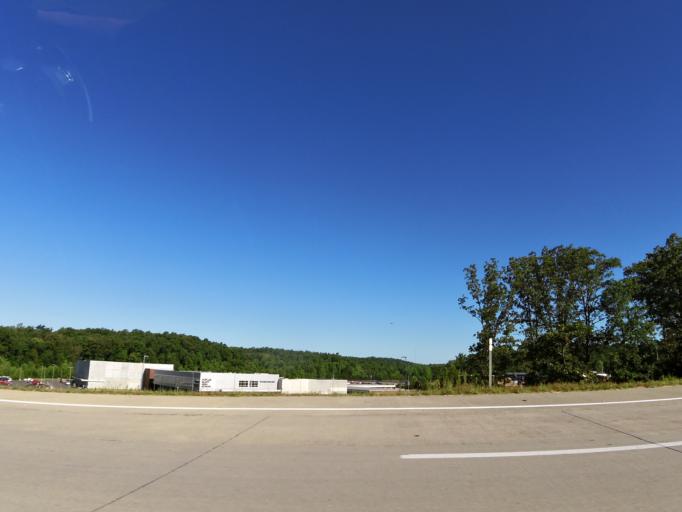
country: US
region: Missouri
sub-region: Butler County
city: Poplar Bluff
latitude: 36.7910
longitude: -90.4484
